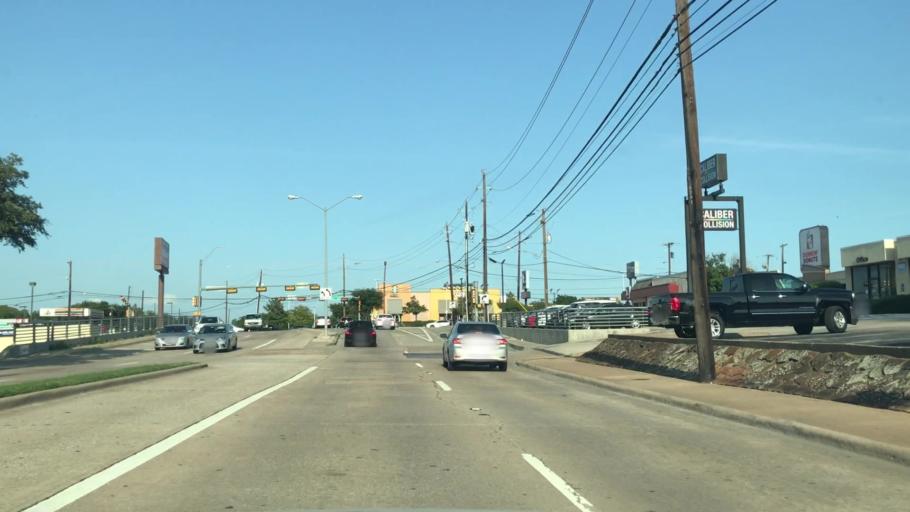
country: US
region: Texas
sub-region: Dallas County
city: Addison
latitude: 32.9328
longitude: -96.8050
